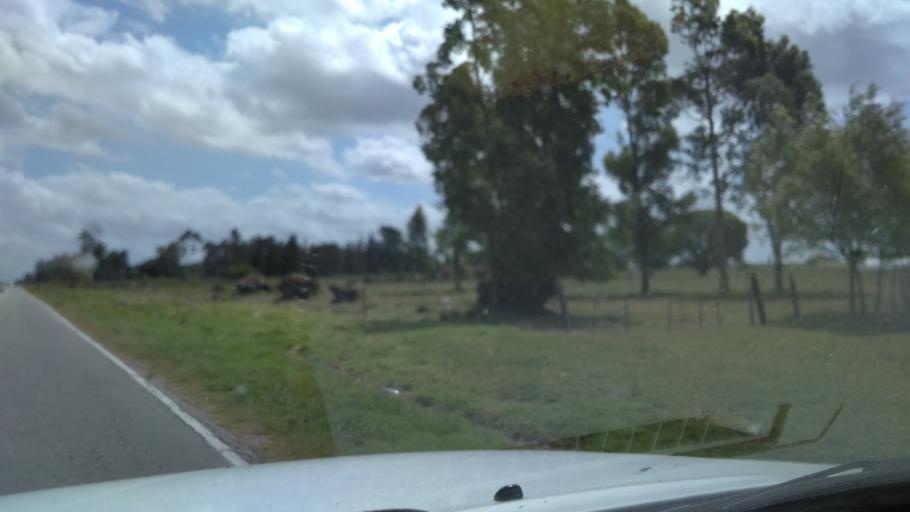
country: UY
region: Canelones
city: San Bautista
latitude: -34.4529
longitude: -55.9850
